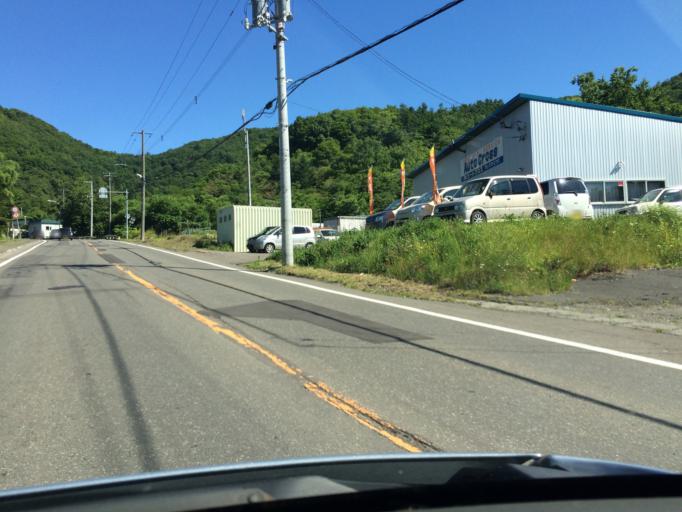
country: JP
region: Hokkaido
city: Sapporo
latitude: 43.0165
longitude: 141.3008
